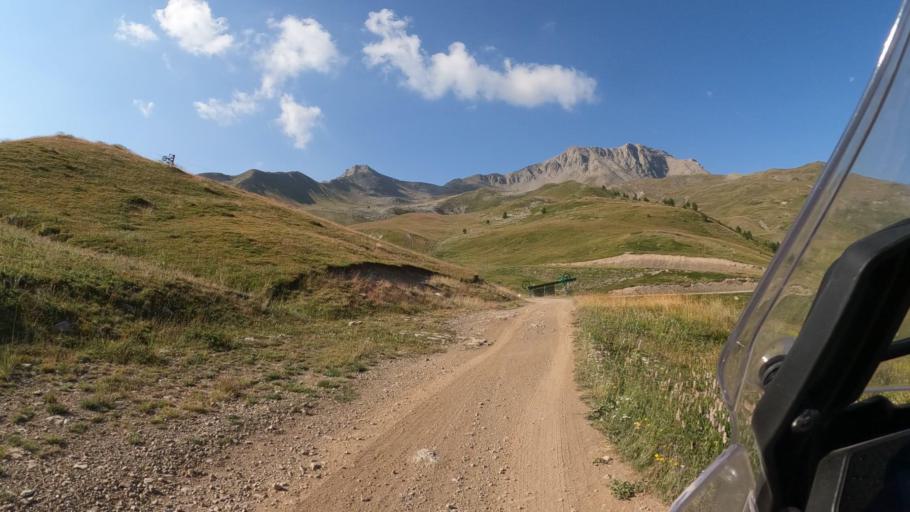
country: FR
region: Provence-Alpes-Cote d'Azur
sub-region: Departement des Hautes-Alpes
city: Guillestre
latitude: 44.5886
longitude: 6.6417
